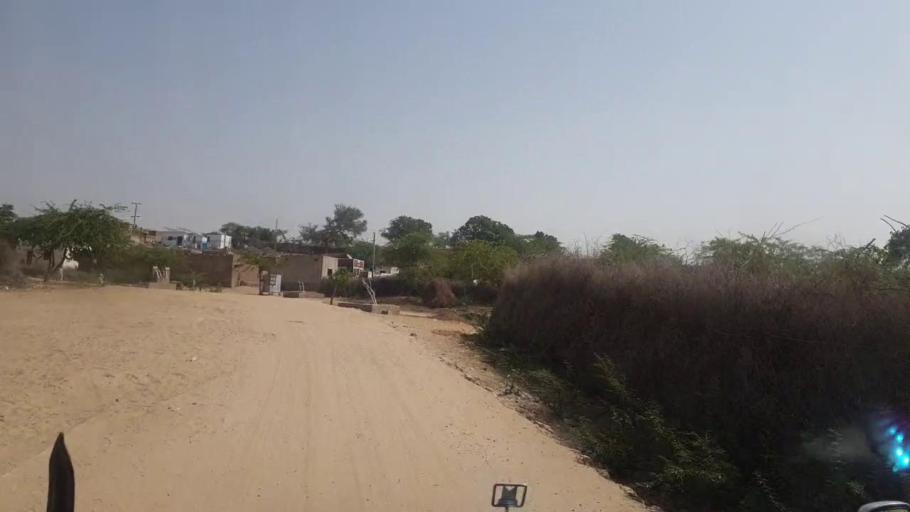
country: PK
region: Sindh
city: Islamkot
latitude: 25.1257
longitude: 70.2121
